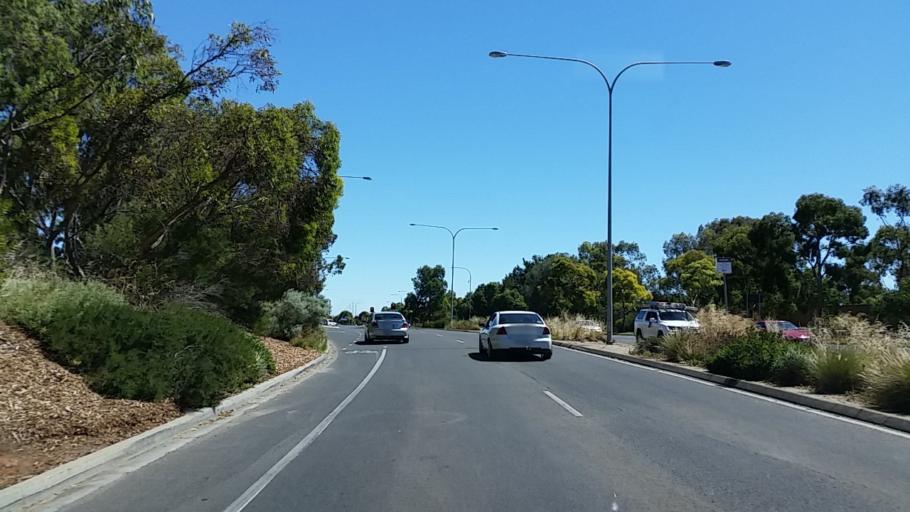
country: AU
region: South Australia
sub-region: City of West Torrens
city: Thebarton
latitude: -34.9291
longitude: 138.5767
